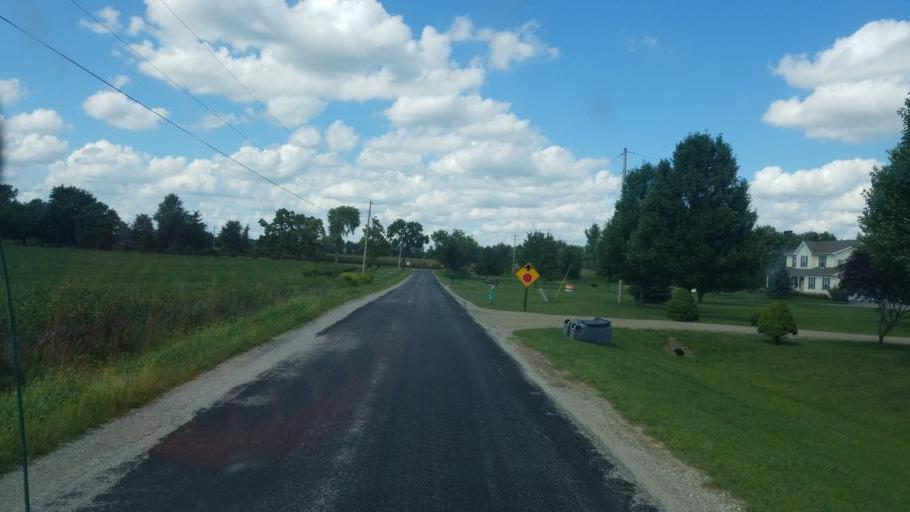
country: US
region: Ohio
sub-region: Union County
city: Richwood
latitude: 40.3140
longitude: -83.2219
